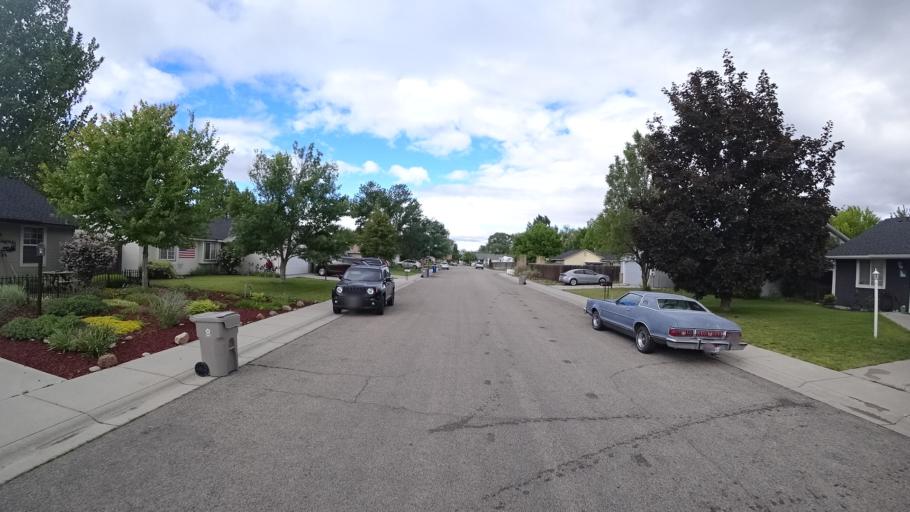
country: US
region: Idaho
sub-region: Ada County
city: Eagle
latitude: 43.6784
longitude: -116.2853
